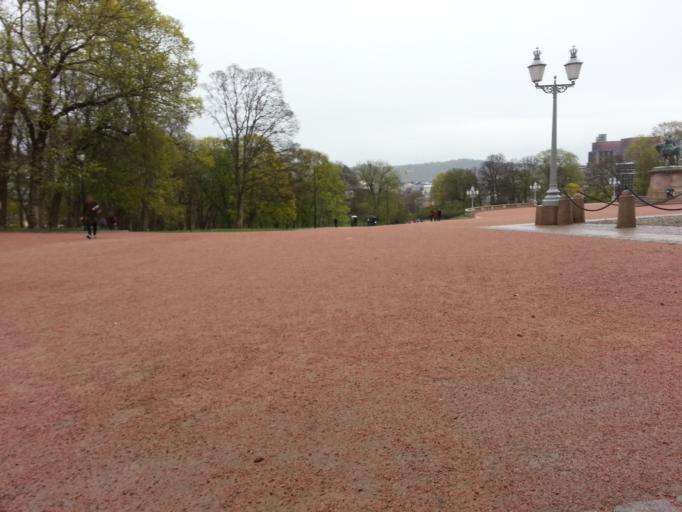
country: NO
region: Oslo
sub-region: Oslo
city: Oslo
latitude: 59.9175
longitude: 10.7283
